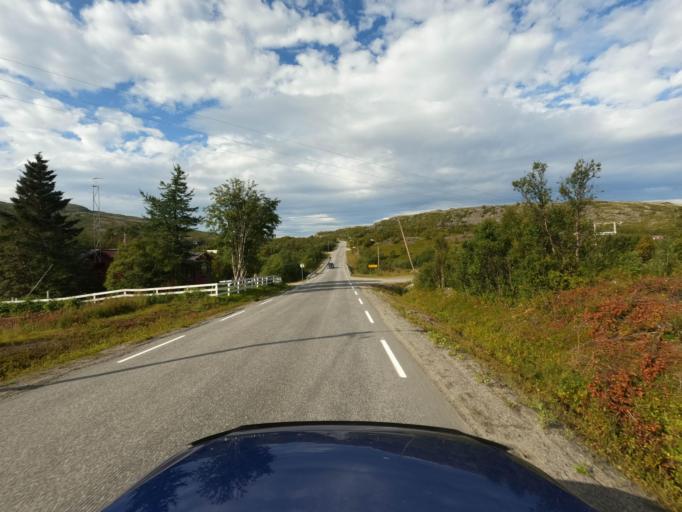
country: NO
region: Finnmark Fylke
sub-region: Kvalsund
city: Kvalsund
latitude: 70.4781
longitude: 24.2150
